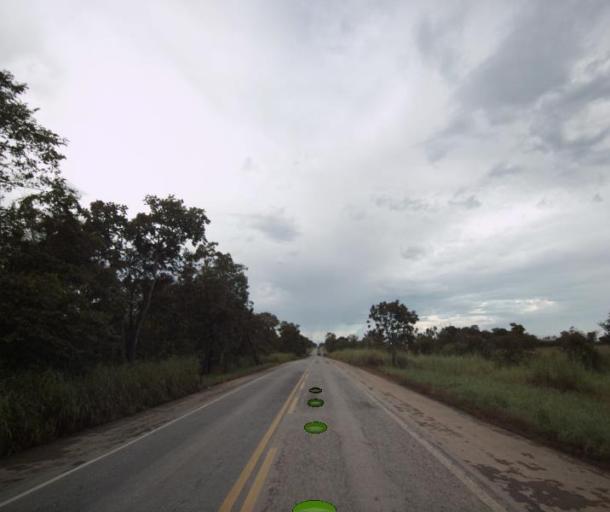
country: BR
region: Goias
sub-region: Porangatu
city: Porangatu
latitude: -13.5999
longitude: -49.0419
